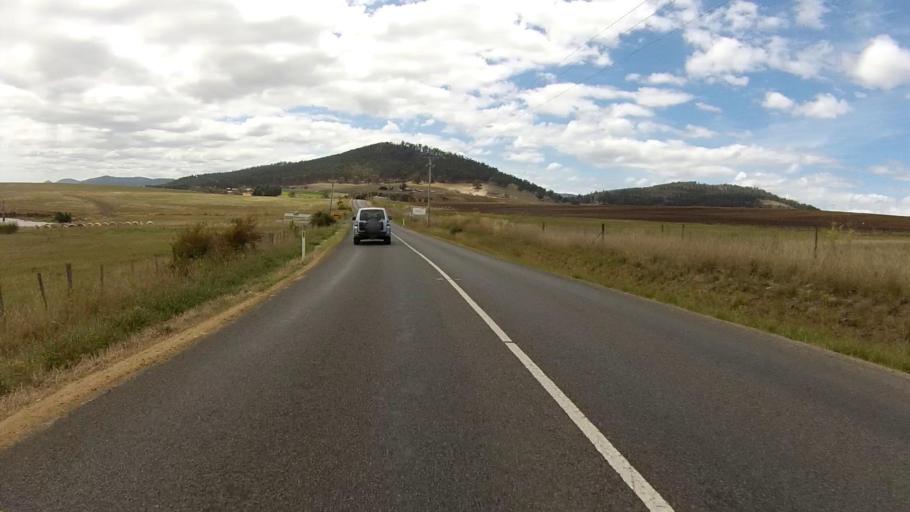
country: AU
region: Tasmania
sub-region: Sorell
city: Sorell
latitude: -42.8072
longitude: 147.6128
